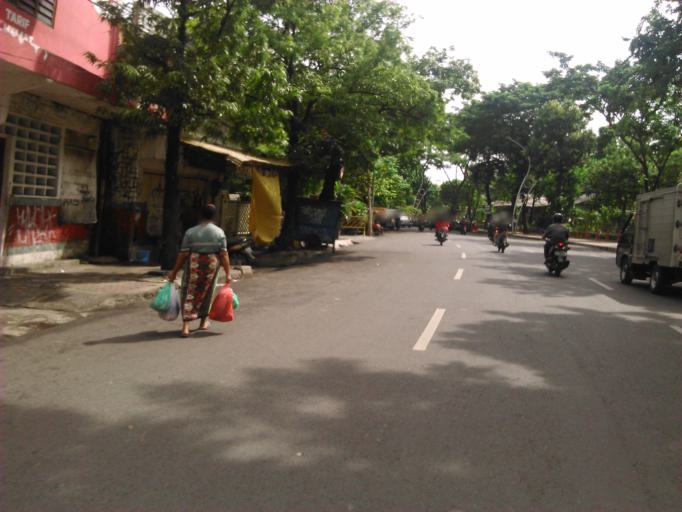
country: ID
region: East Java
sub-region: Kota Surabaya
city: Surabaya
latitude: -7.2584
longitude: 112.7434
